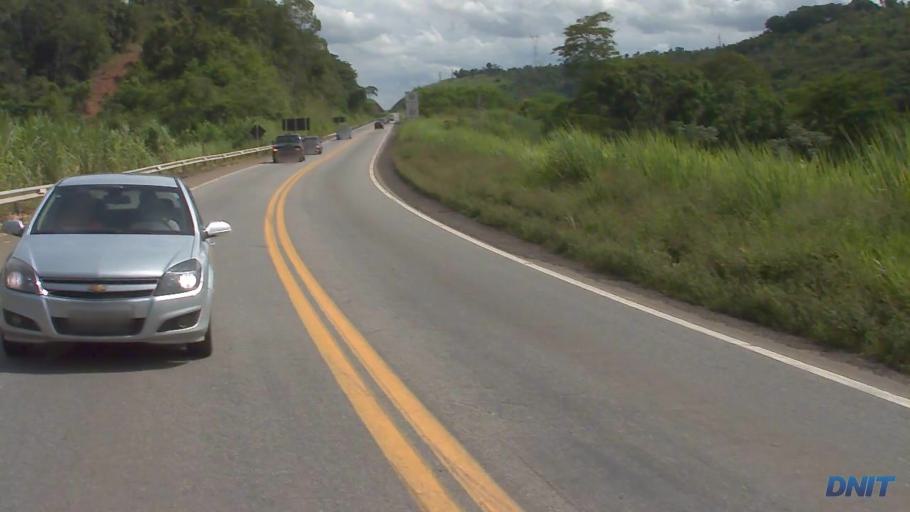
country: BR
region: Minas Gerais
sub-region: Ipaba
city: Ipaba
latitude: -19.4075
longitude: -42.4867
